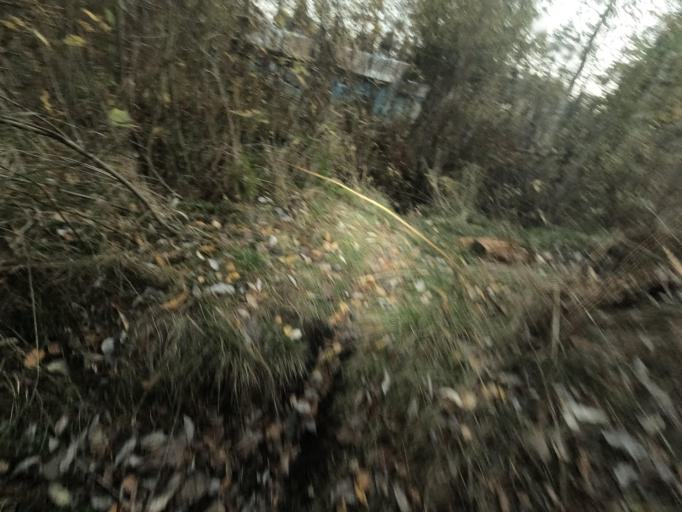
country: RU
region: St.-Petersburg
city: Komarovo
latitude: 60.2005
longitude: 29.8158
